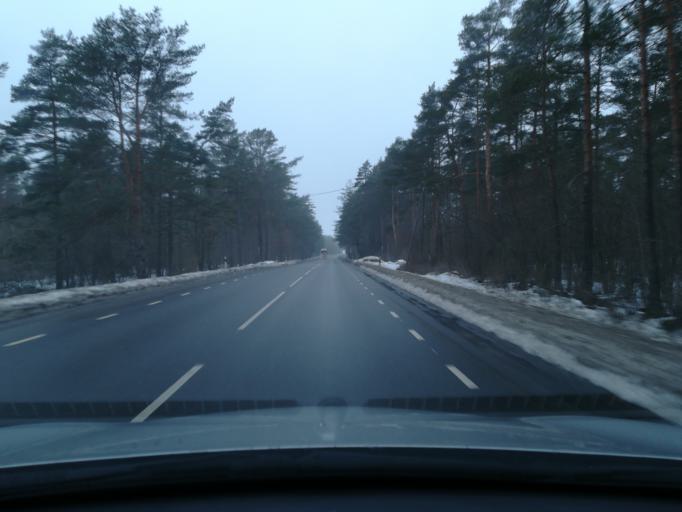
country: EE
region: Harju
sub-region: Raasiku vald
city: Arukula
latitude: 59.3577
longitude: 25.0635
